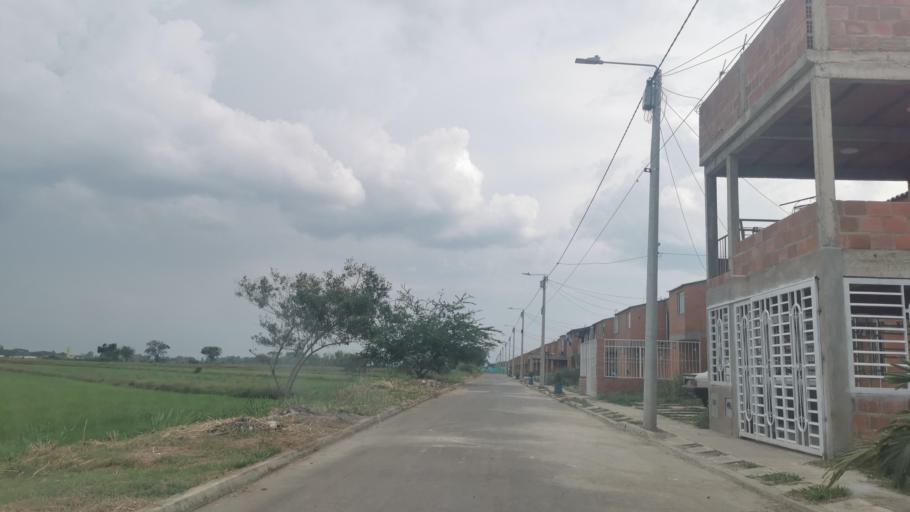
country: CO
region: Valle del Cauca
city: Jamundi
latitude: 3.2346
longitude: -76.5245
